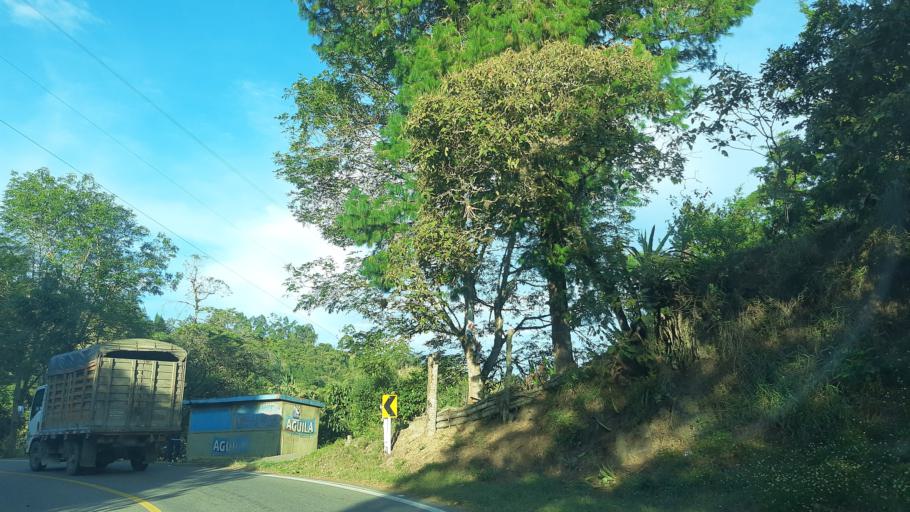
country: CO
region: Boyaca
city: Guateque
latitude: 5.0051
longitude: -73.4971
